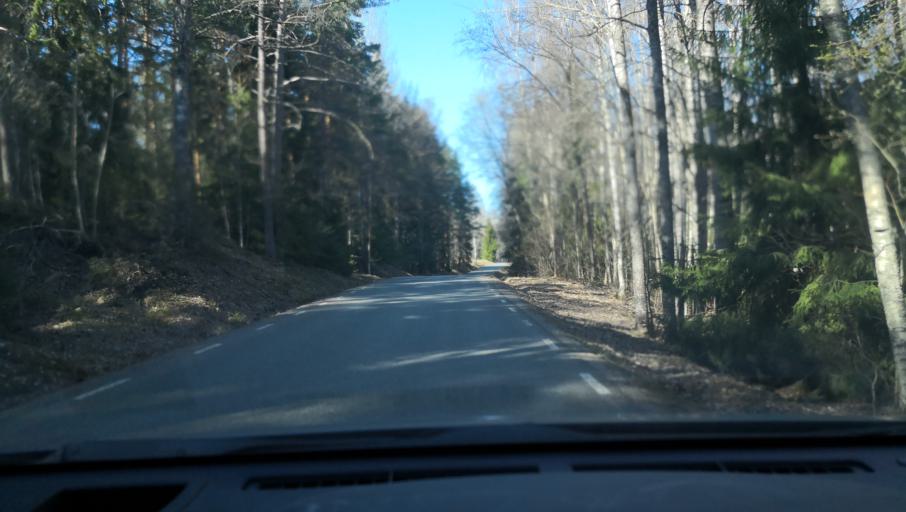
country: SE
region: Vaestmanland
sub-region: Sala Kommun
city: Sala
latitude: 59.9812
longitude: 16.4748
